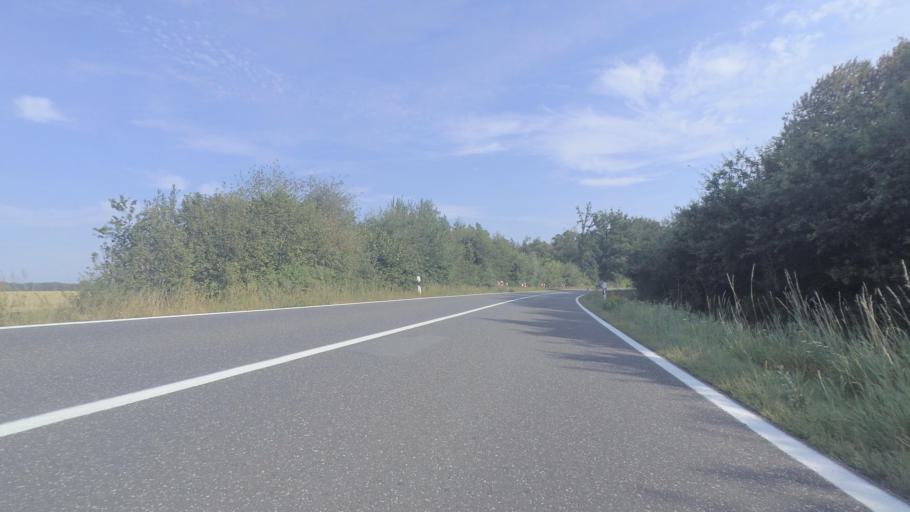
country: DE
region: Mecklenburg-Vorpommern
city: Grimmen
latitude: 54.0775
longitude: 13.1099
